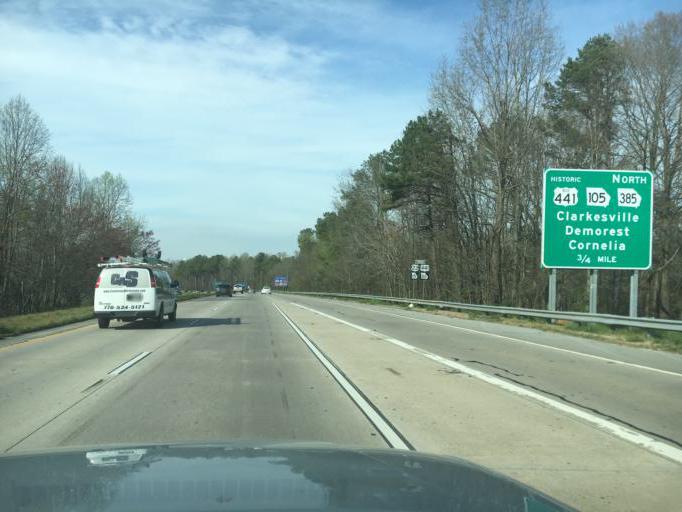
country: US
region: Georgia
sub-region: Habersham County
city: Cornelia
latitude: 34.5229
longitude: -83.5421
